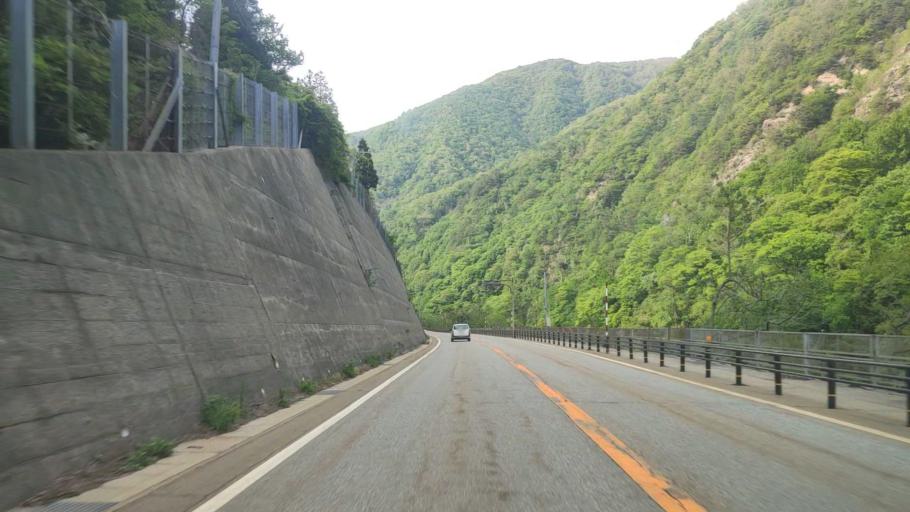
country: JP
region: Gifu
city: Takayama
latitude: 36.3551
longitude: 137.2879
